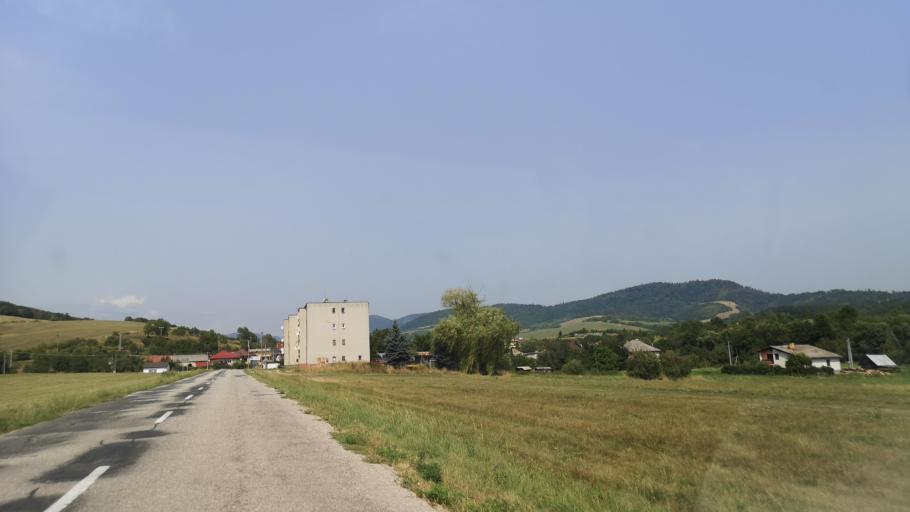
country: SK
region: Kosicky
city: Dobsina
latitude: 48.6866
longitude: 20.3484
